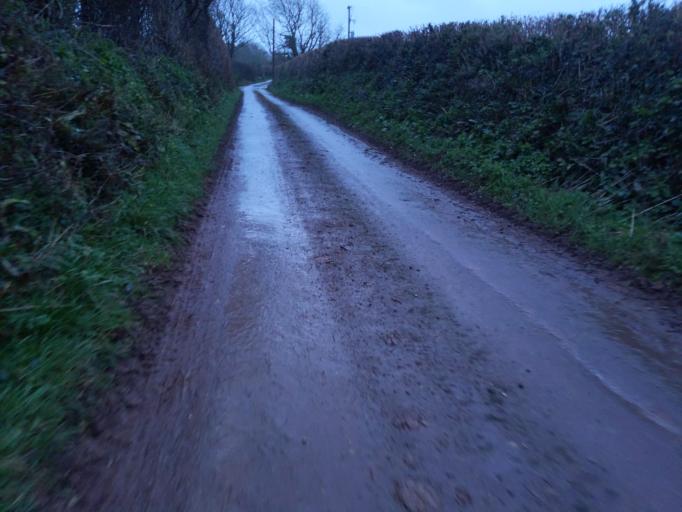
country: GB
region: England
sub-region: Devon
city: Yealmpton
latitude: 50.3330
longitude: -4.0185
